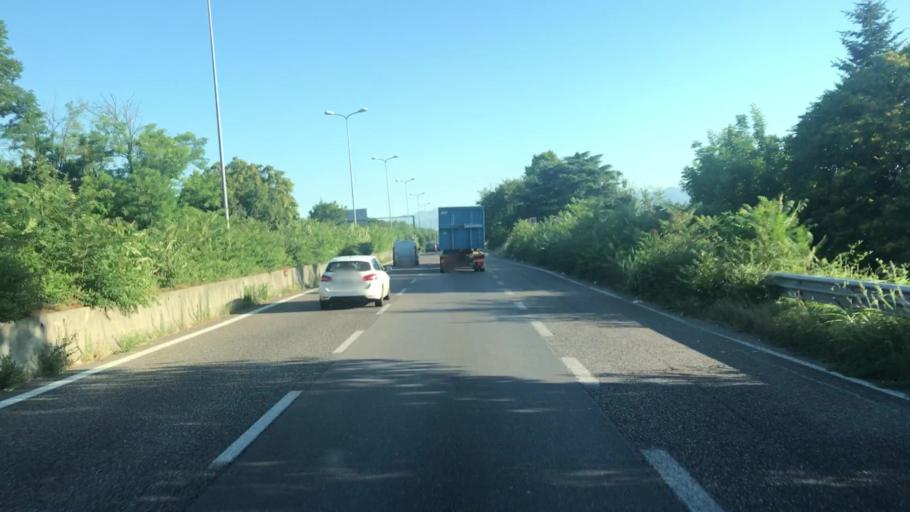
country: IT
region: Lombardy
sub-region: Provincia di Monza e Brianza
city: Cesano Maderno
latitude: 45.6386
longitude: 9.1589
